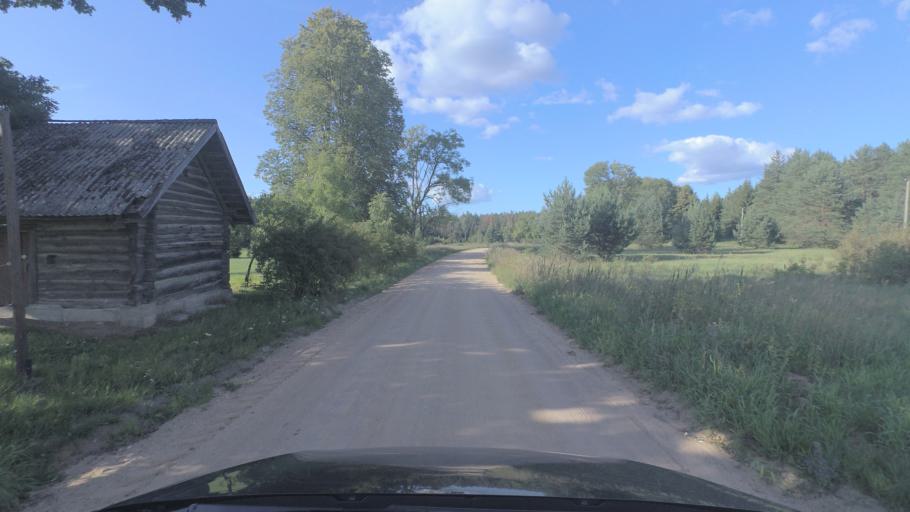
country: LT
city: Pabrade
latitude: 55.1409
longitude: 25.7369
